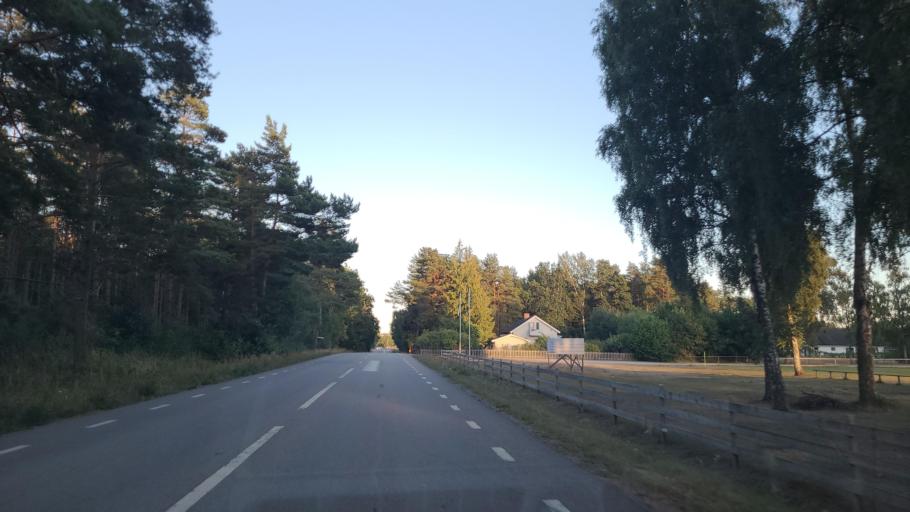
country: SE
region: Kalmar
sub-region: Borgholms Kommun
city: Borgholm
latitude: 57.2577
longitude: 17.0457
